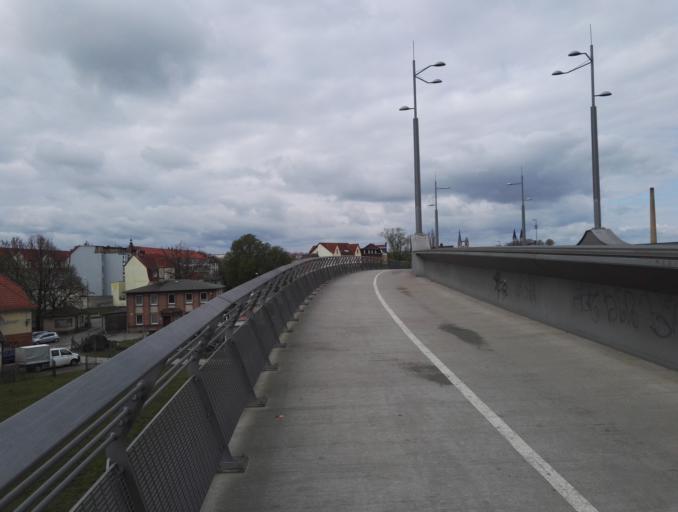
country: DE
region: Saxony-Anhalt
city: Halberstadt
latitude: 51.9001
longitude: 11.0702
